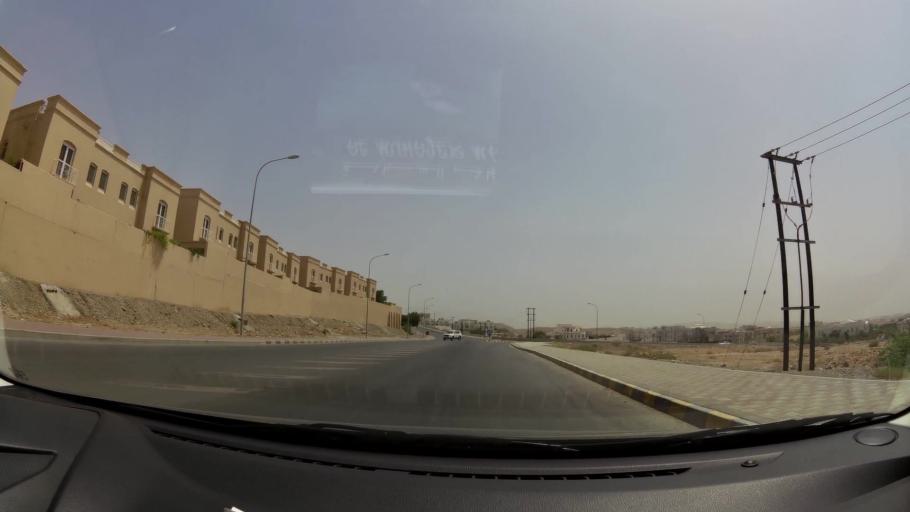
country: OM
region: Muhafazat Masqat
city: Bawshar
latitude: 23.5601
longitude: 58.3995
